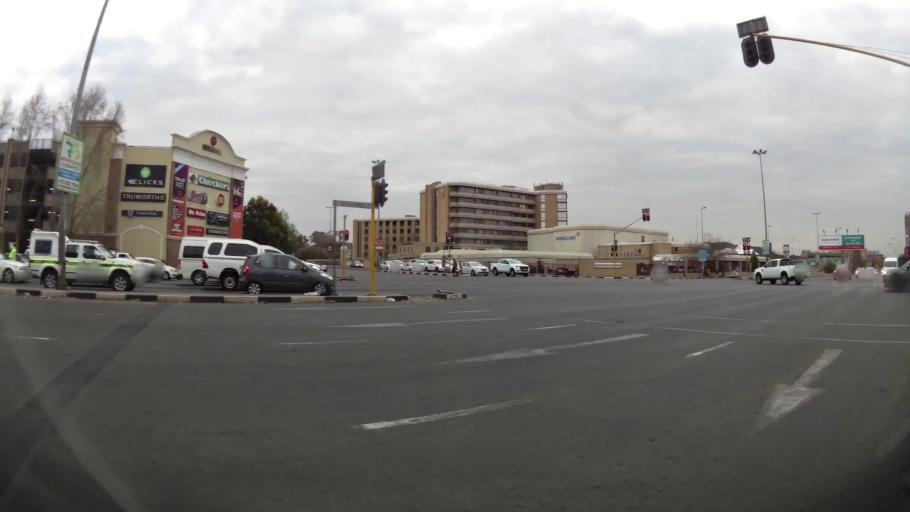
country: ZA
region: Orange Free State
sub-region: Mangaung Metropolitan Municipality
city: Bloemfontein
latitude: -29.1103
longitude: 26.2018
